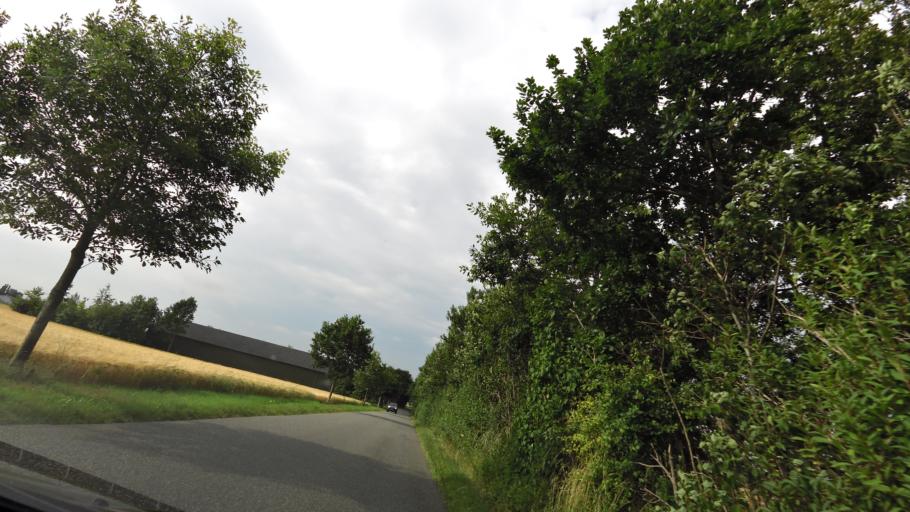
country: DK
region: South Denmark
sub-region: Nordfyns Kommune
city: Otterup
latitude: 55.5595
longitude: 10.4224
